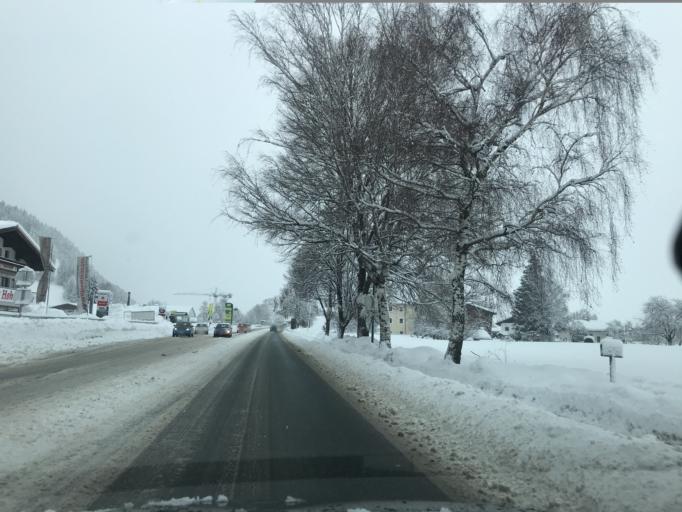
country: AT
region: Salzburg
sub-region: Politischer Bezirk Zell am See
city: Maishofen
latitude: 47.3580
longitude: 12.7999
